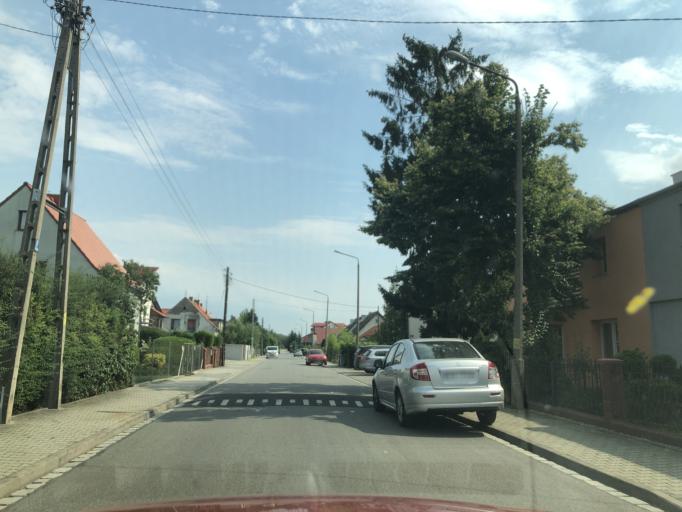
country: PL
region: Lower Silesian Voivodeship
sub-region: Powiat wroclawski
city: Smolec
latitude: 51.1562
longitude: 16.9120
